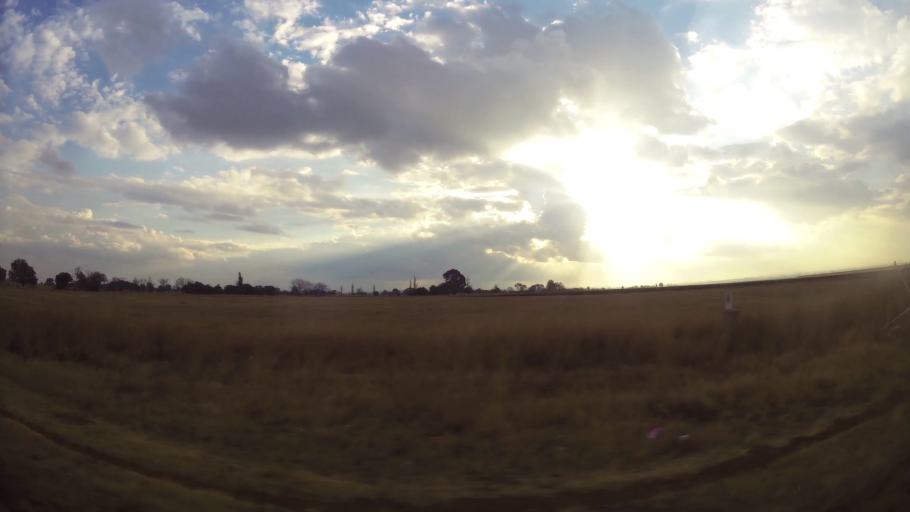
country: ZA
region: Gauteng
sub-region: Sedibeng District Municipality
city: Vanderbijlpark
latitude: -26.6274
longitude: 27.8099
